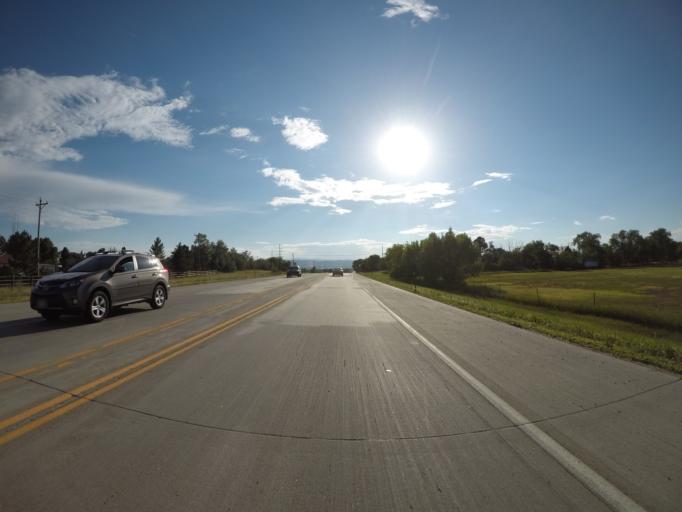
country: US
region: Colorado
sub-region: Larimer County
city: Fort Collins
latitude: 40.5812
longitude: -104.9773
